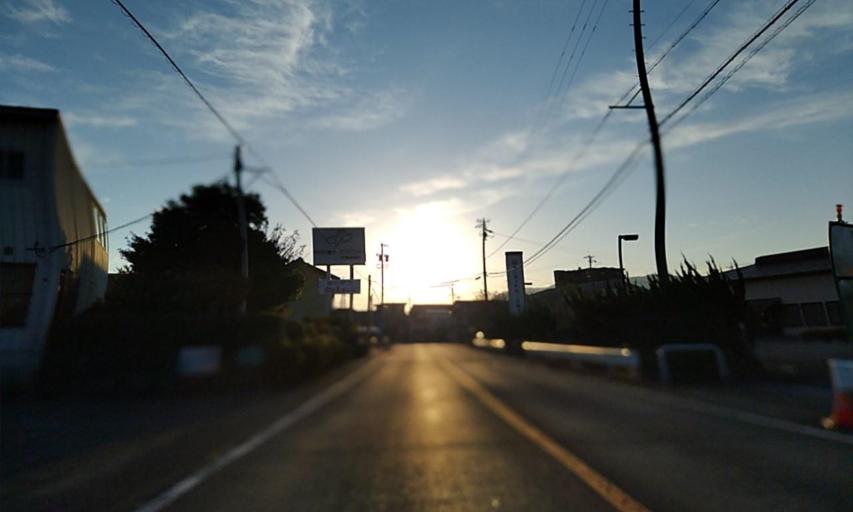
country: JP
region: Mie
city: Ise
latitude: 34.4967
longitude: 136.7251
